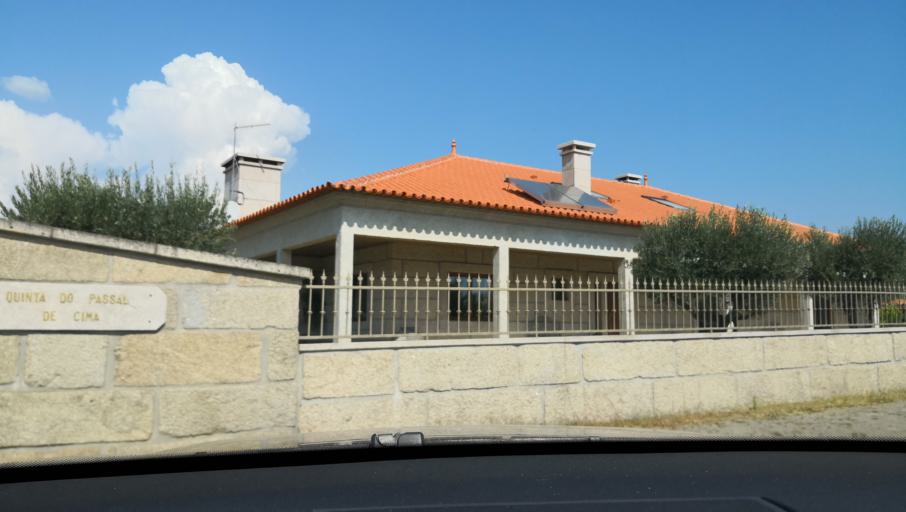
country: PT
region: Vila Real
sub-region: Sabrosa
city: Sabrosa
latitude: 41.2656
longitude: -7.6108
